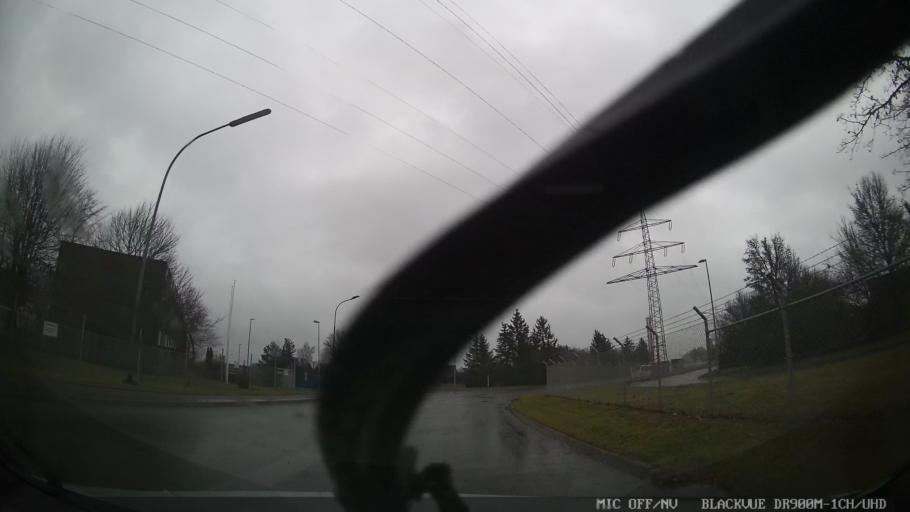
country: DE
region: Rheinland-Pfalz
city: Idar-Oberstein
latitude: 49.7133
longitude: 7.2939
